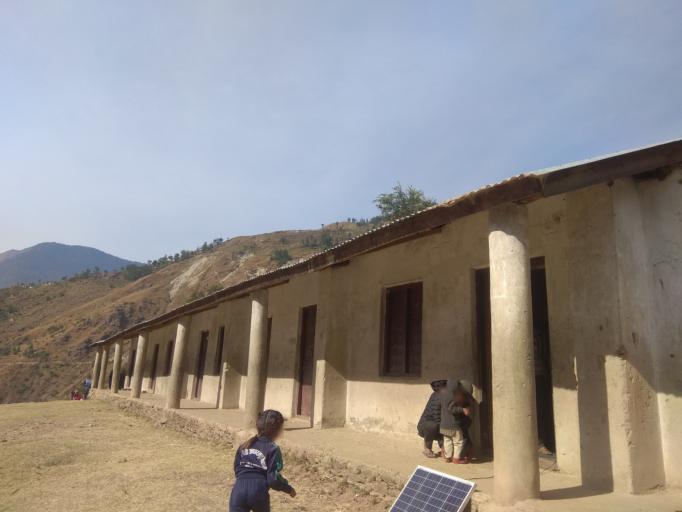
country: NP
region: Mid Western
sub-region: Bheri Zone
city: Dailekh
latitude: 29.2389
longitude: 81.6595
